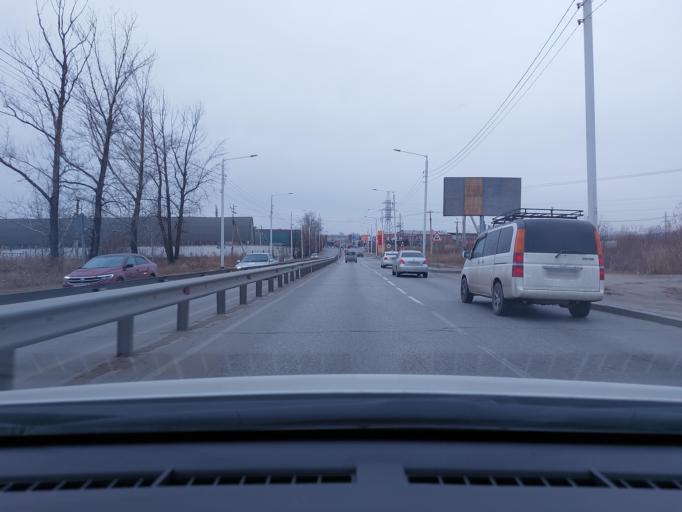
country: RU
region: Irkutsk
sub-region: Irkutskiy Rayon
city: Irkutsk
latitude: 52.3347
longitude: 104.2333
